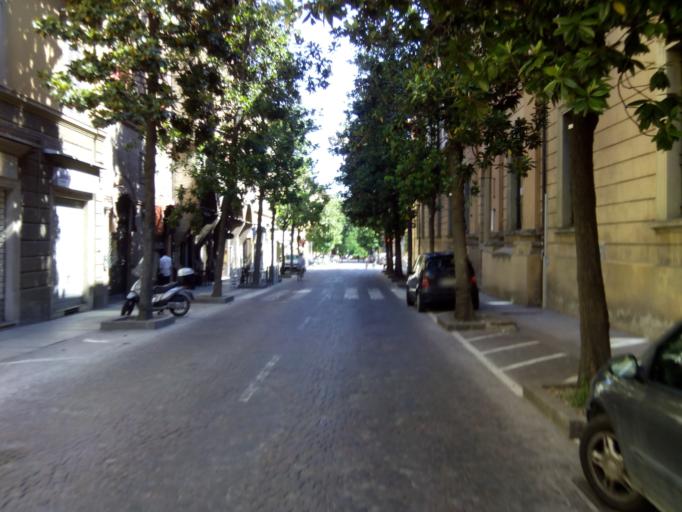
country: IT
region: Emilia-Romagna
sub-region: Provincia di Bologna
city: Bologna
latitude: 44.4887
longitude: 11.3431
